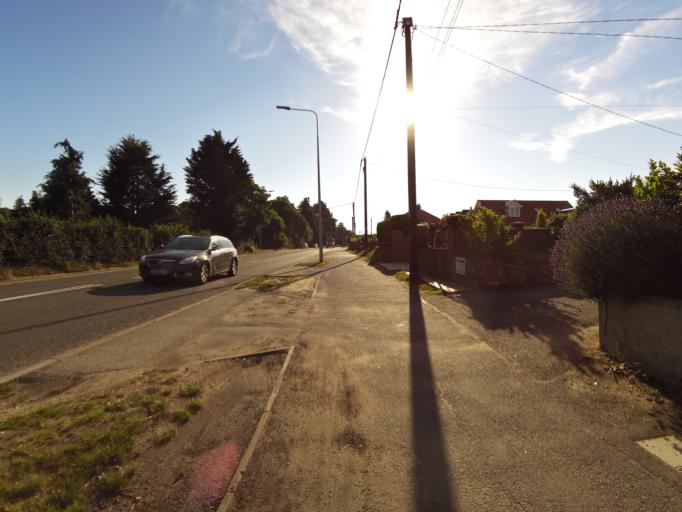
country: GB
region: England
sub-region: Suffolk
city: Kesgrave
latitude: 52.0677
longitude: 1.2578
